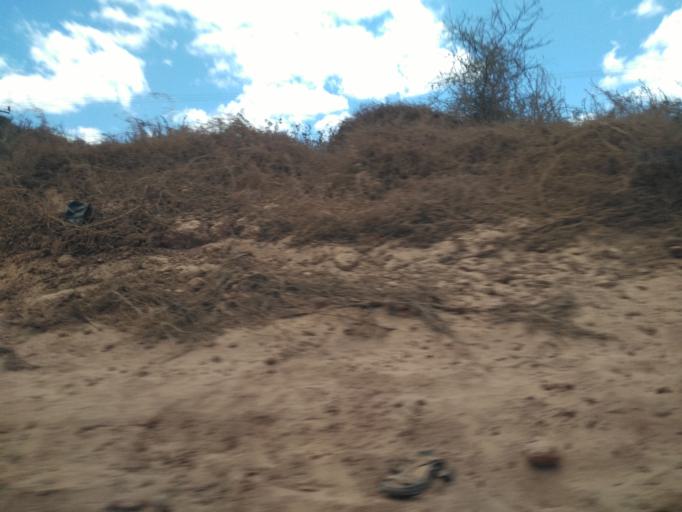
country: TZ
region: Dodoma
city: Dodoma
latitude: -6.2056
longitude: 35.7549
